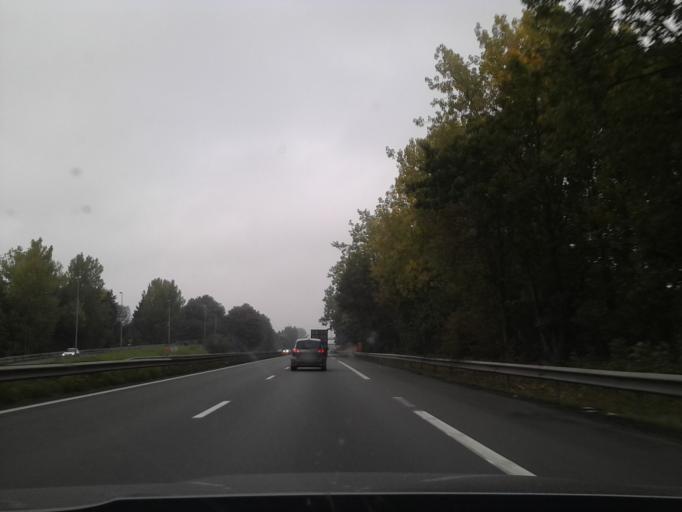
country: FR
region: Nord-Pas-de-Calais
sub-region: Departement du Nord
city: Lieu-Saint-Amand
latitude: 50.2694
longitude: 3.3336
